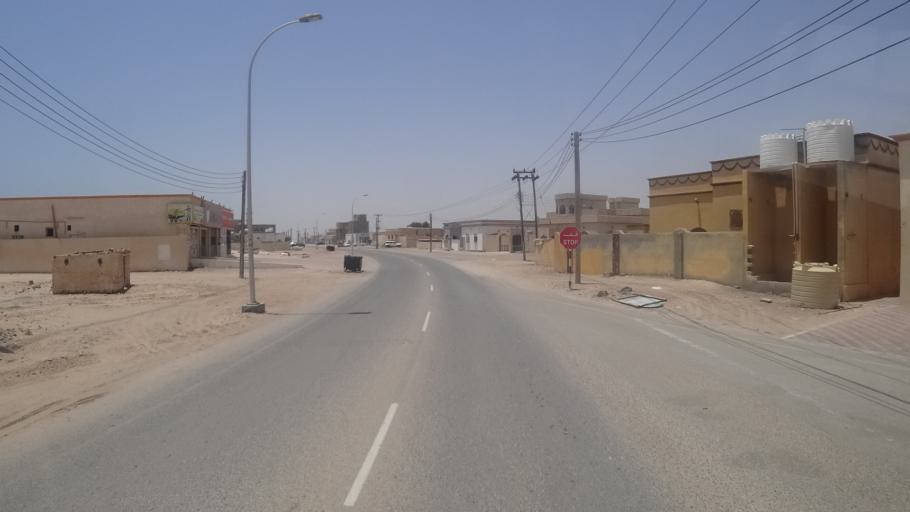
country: OM
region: Ash Sharqiyah
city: Sur
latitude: 22.0843
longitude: 59.6861
